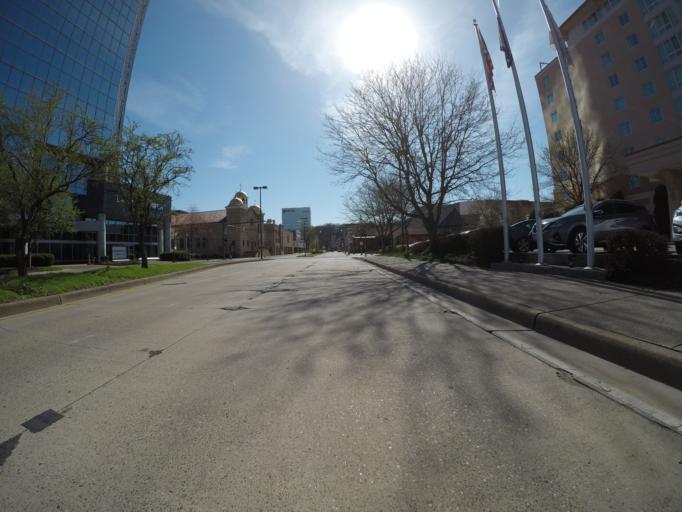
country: US
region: West Virginia
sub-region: Kanawha County
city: Charleston
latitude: 38.3537
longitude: -81.6349
